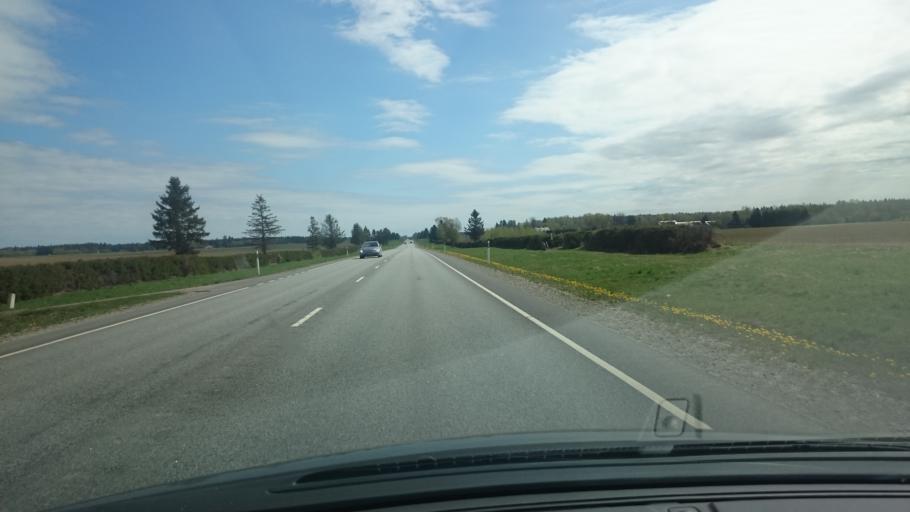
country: EE
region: Laeaene-Virumaa
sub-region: Someru vald
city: Someru
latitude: 59.3664
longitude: 26.4810
